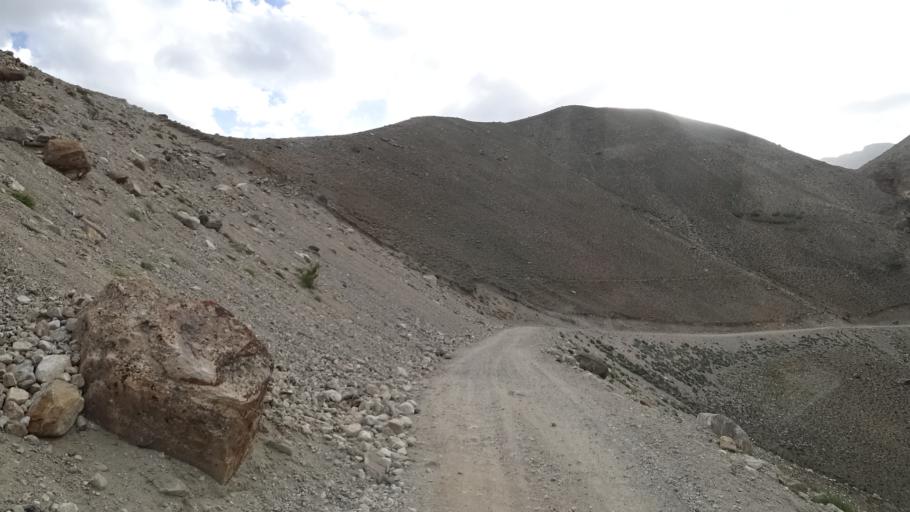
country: AF
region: Badakhshan
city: Khandud
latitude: 37.2187
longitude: 72.7889
